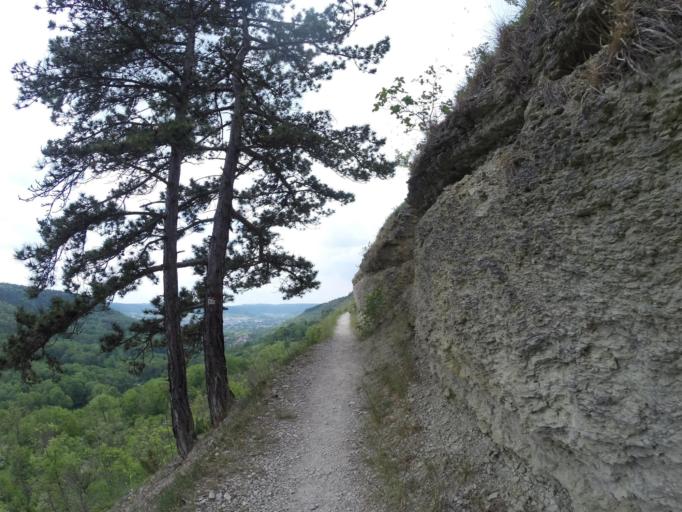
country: DE
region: Thuringia
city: Jena
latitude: 50.9084
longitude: 11.6197
